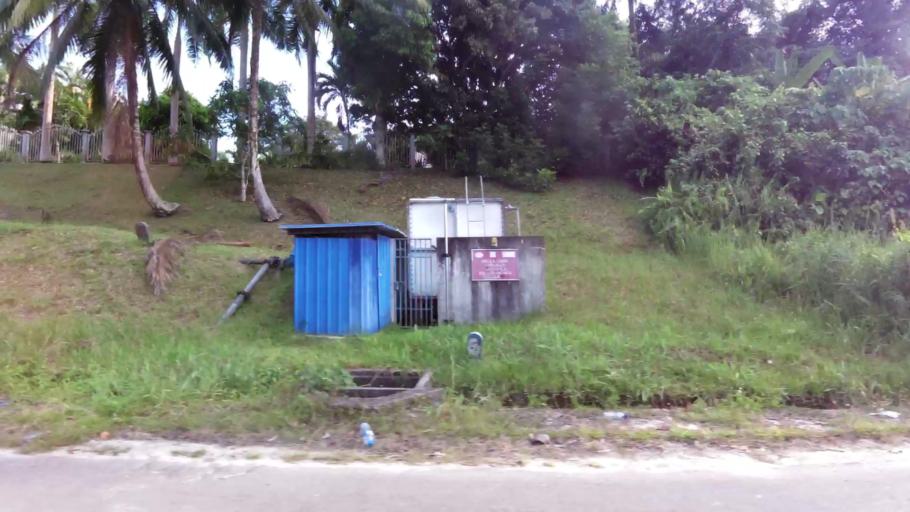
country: BN
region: Brunei and Muara
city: Bandar Seri Begawan
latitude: 4.9645
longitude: 114.9839
